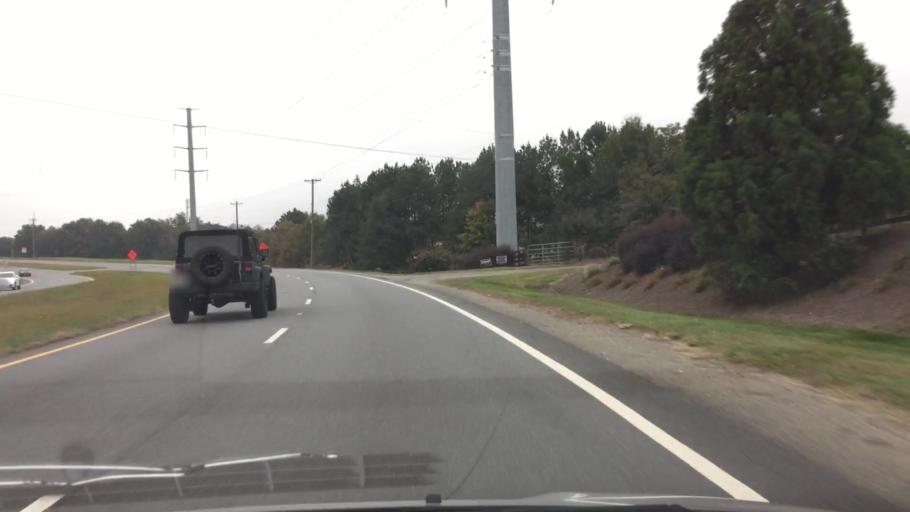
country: US
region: Georgia
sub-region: Fulton County
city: Milton
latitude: 34.1317
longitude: -84.2369
